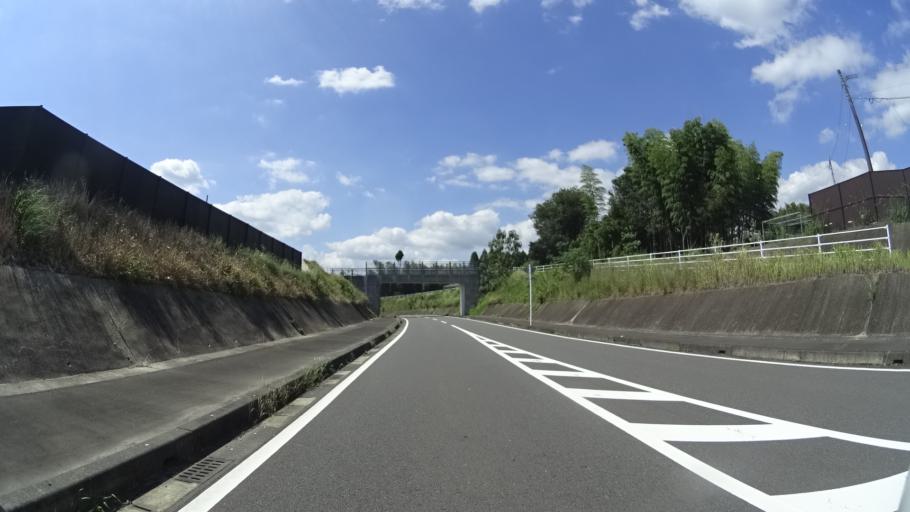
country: JP
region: Kagoshima
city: Kajiki
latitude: 31.8151
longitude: 130.7017
